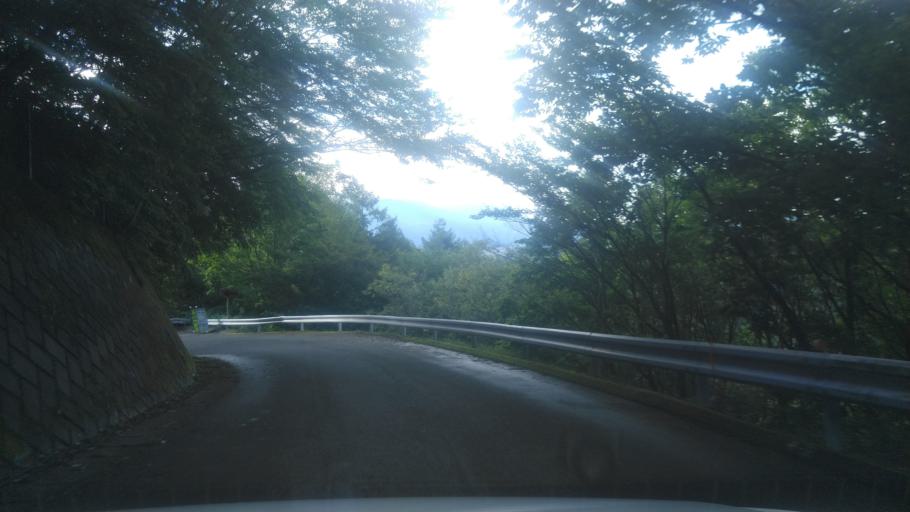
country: JP
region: Nagano
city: Suzaka
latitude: 36.5429
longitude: 138.2990
